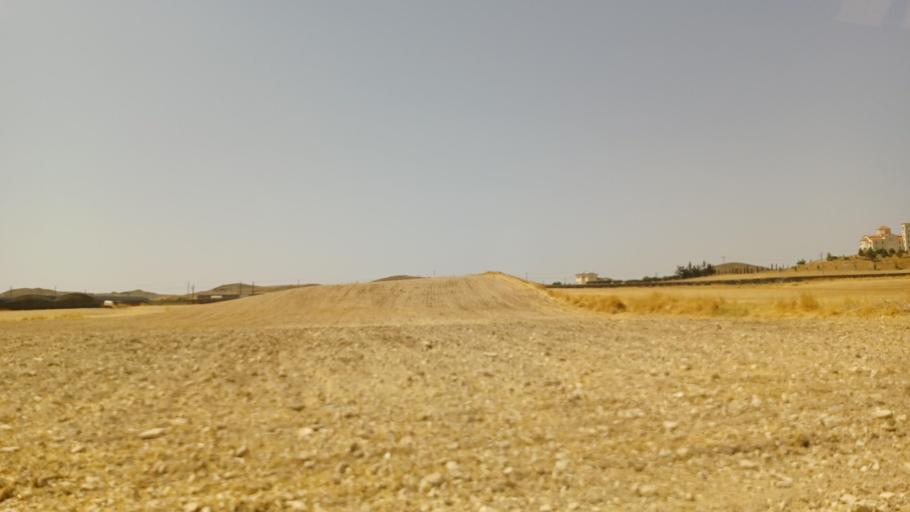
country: CY
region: Larnaka
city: Troulloi
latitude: 35.0304
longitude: 33.5975
